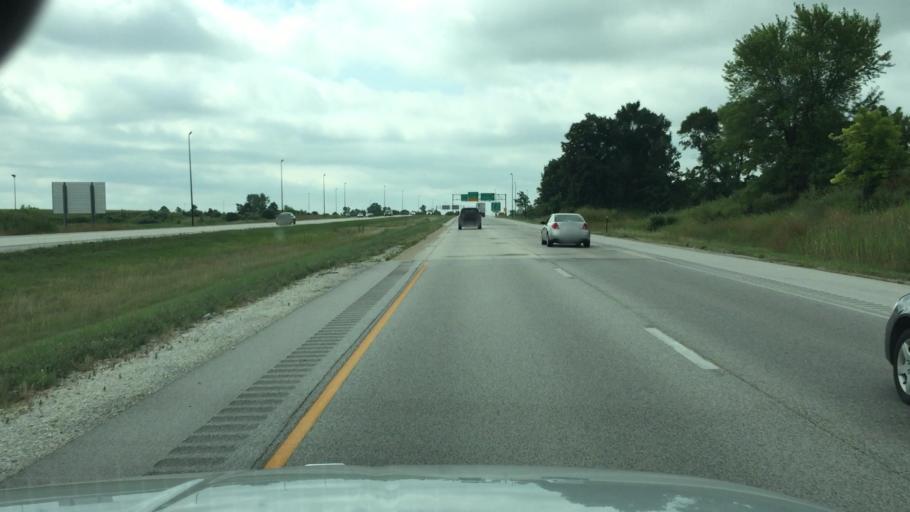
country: US
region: Illinois
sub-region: Henry County
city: Green Rock
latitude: 41.4475
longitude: -90.3332
